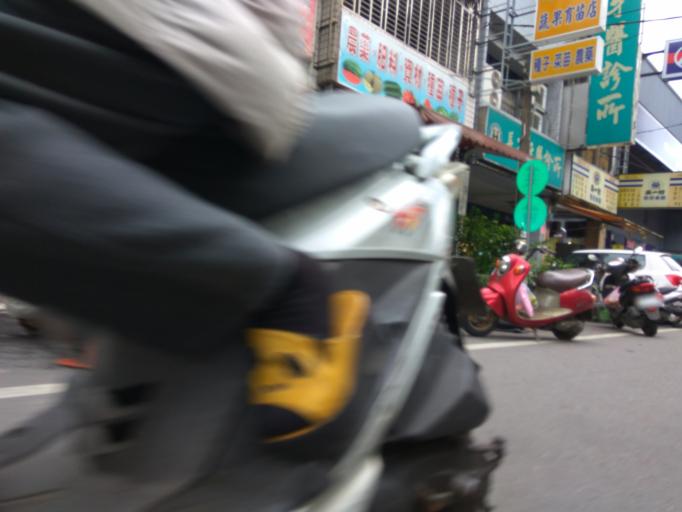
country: TW
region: Taiwan
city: Taoyuan City
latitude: 24.9570
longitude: 121.2152
